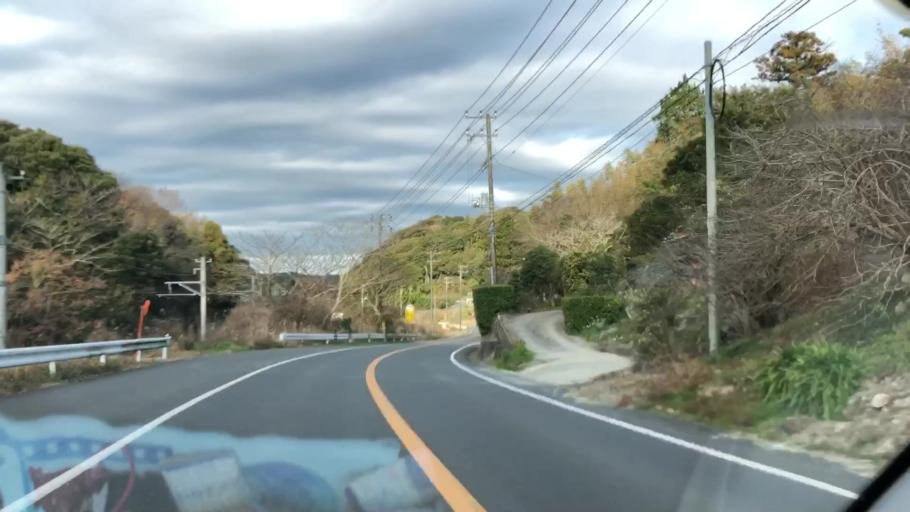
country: JP
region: Chiba
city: Tateyama
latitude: 34.9891
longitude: 139.9282
